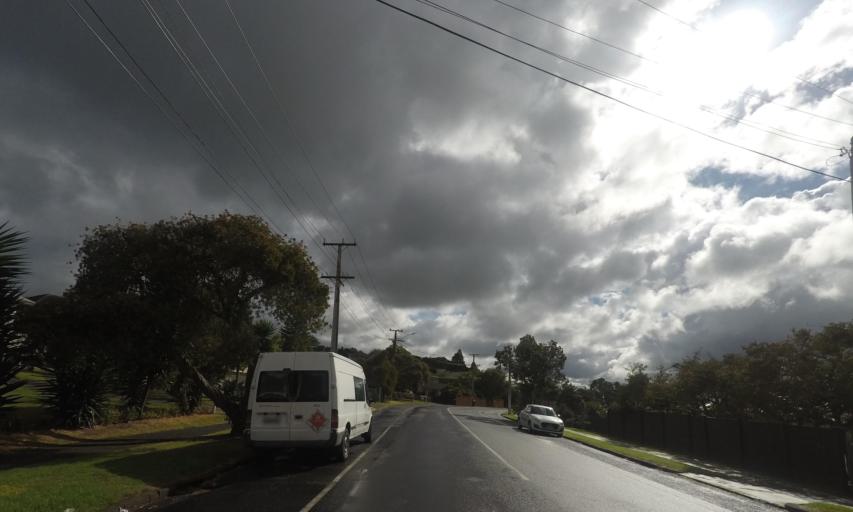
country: NZ
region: Auckland
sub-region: Auckland
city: Mangere
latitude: -36.9517
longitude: 174.7867
